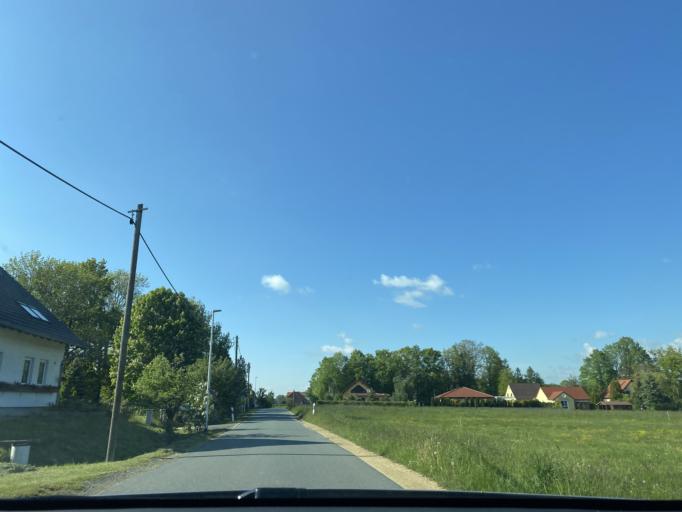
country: DE
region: Saxony
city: Reichenbach
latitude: 51.1012
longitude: 14.8318
